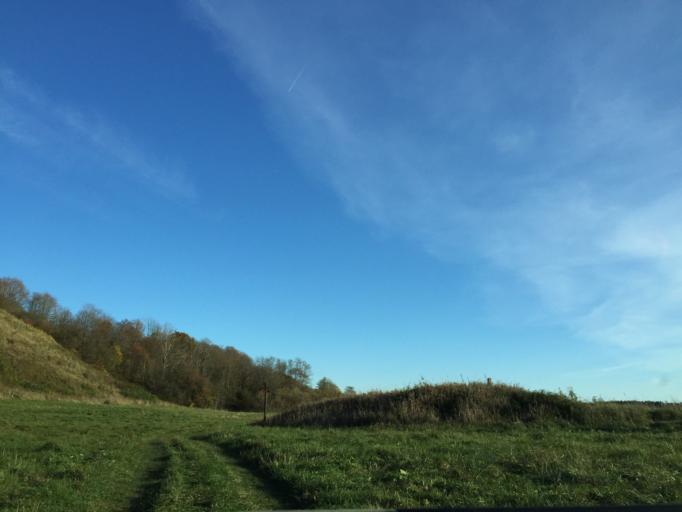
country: LV
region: Skriveri
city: Skriveri
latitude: 56.6213
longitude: 25.1281
